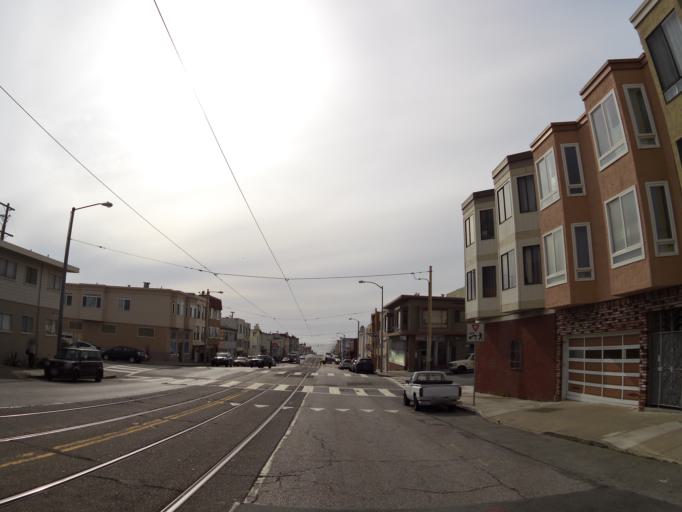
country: US
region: California
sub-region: San Mateo County
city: Daly City
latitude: 37.7422
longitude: -122.4967
